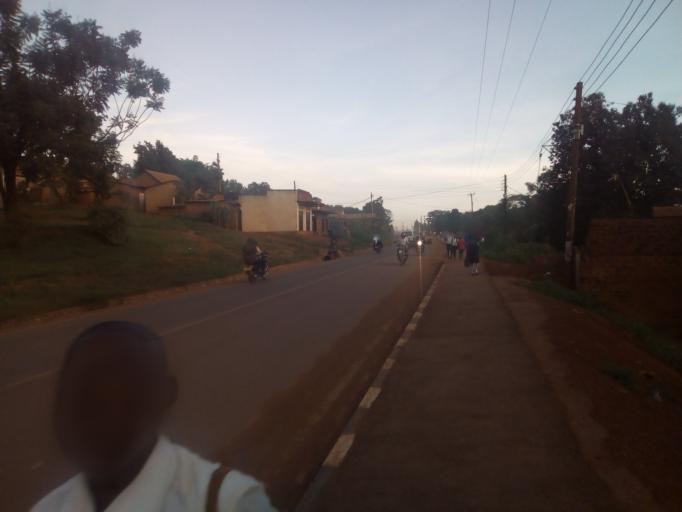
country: UG
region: Central Region
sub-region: Wakiso District
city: Kajansi
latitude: 0.2406
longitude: 32.5733
